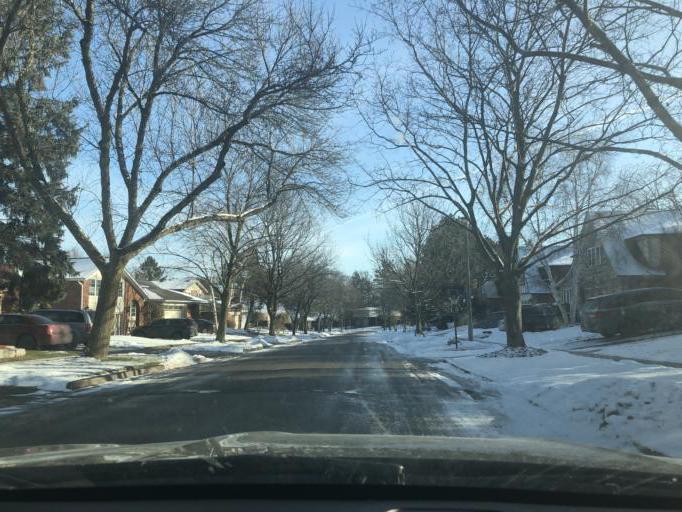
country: CA
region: Ontario
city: Scarborough
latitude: 43.7738
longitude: -79.1528
